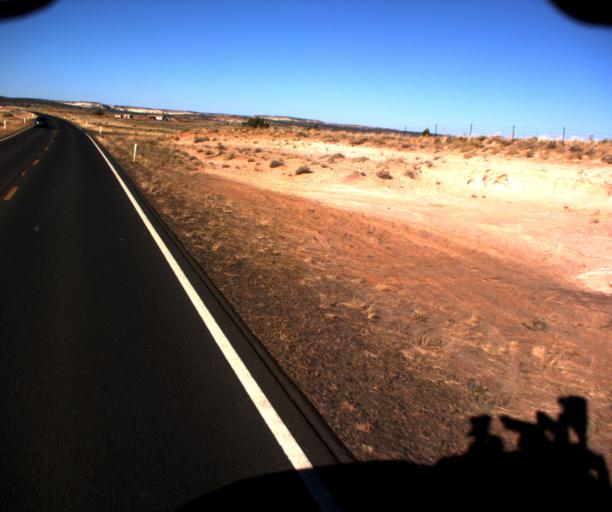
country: US
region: Arizona
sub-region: Apache County
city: Ganado
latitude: 35.7837
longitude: -109.7138
